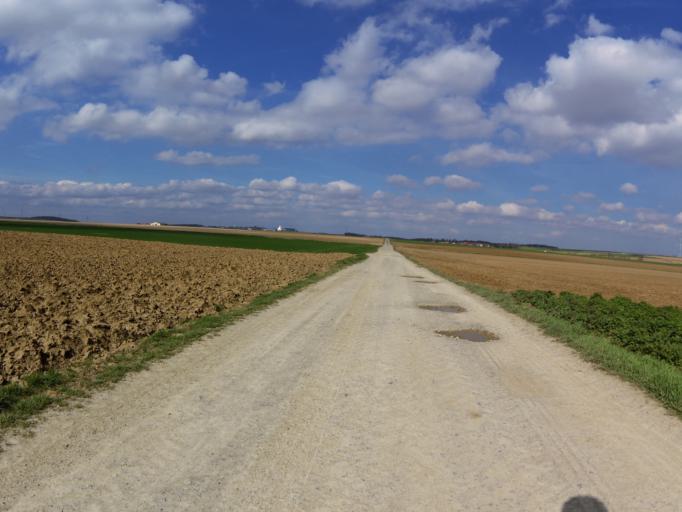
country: DE
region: Bavaria
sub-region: Regierungsbezirk Unterfranken
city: Biebelried
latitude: 49.7507
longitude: 10.0882
